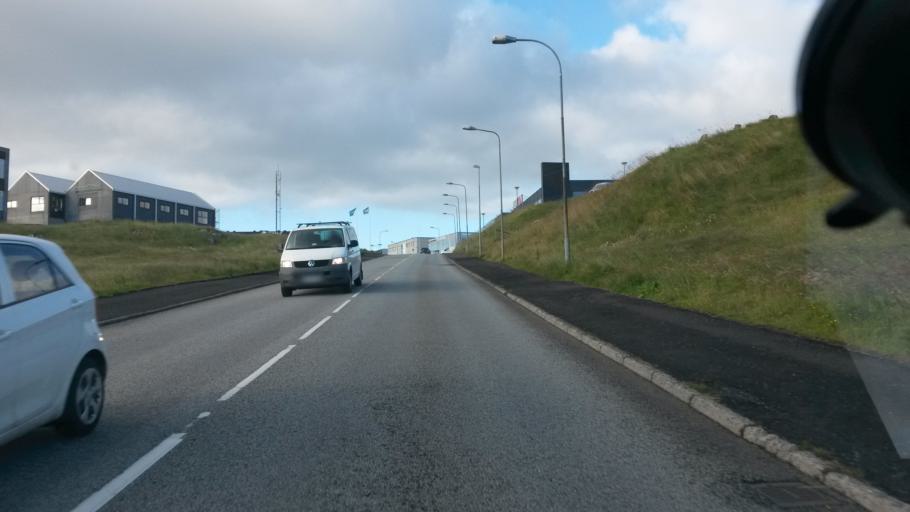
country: FO
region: Streymoy
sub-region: Torshavn
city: Torshavn
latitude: 62.0234
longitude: -6.7630
